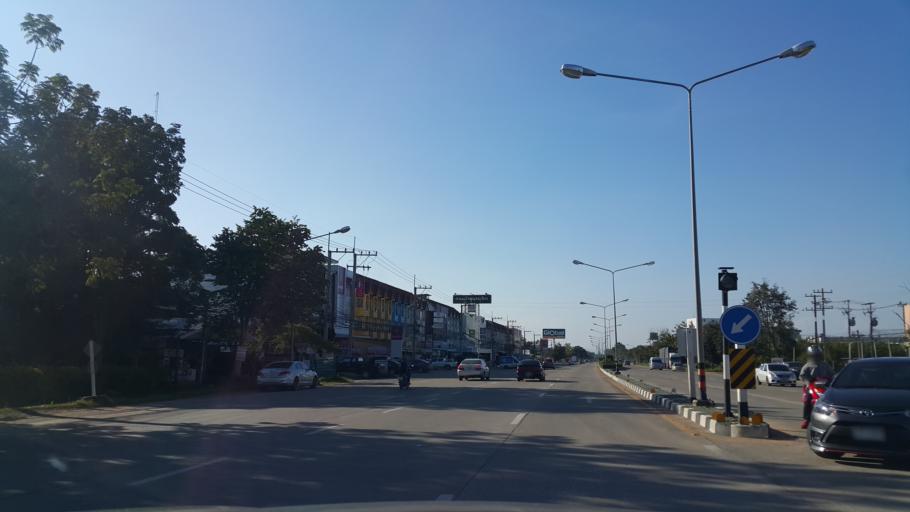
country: TH
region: Lamphun
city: Lamphun
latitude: 18.5583
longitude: 99.0389
